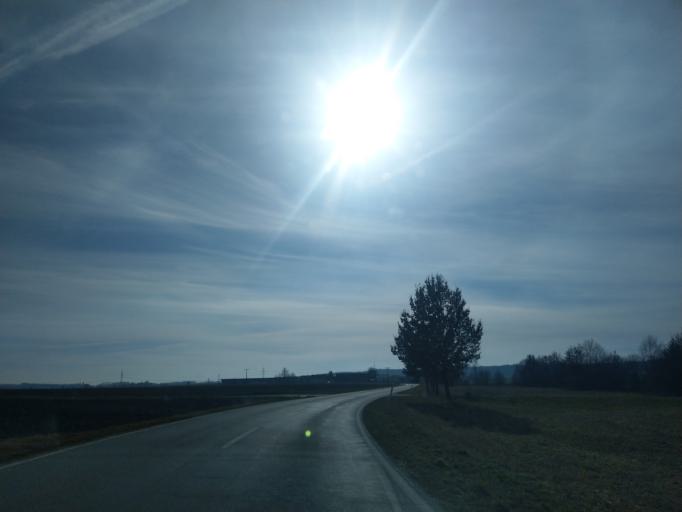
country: DE
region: Bavaria
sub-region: Lower Bavaria
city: Buchhofen
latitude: 48.6770
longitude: 12.9629
